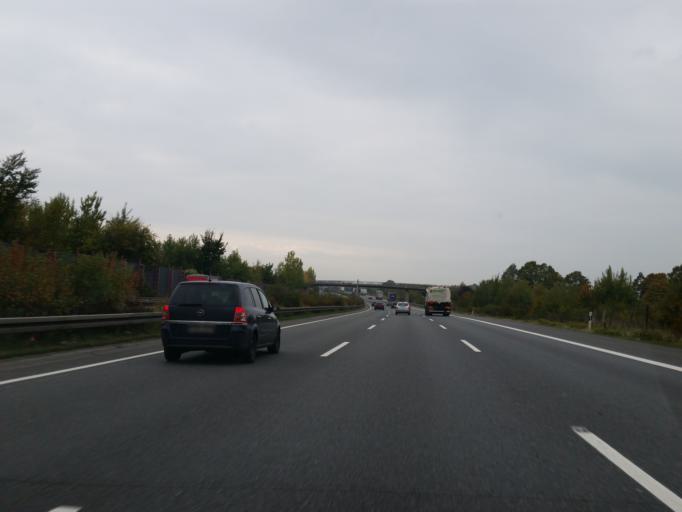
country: DE
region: Lower Saxony
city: Dollbergen
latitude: 52.3542
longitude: 10.1925
